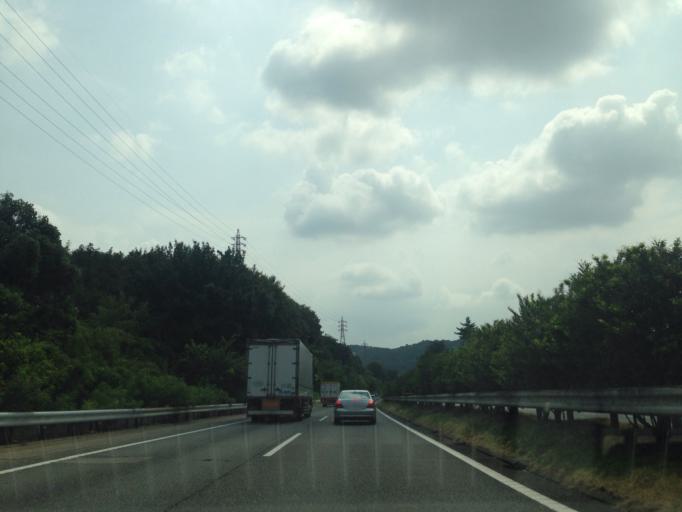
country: JP
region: Aichi
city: Kozakai-cho
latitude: 34.8548
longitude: 137.3407
